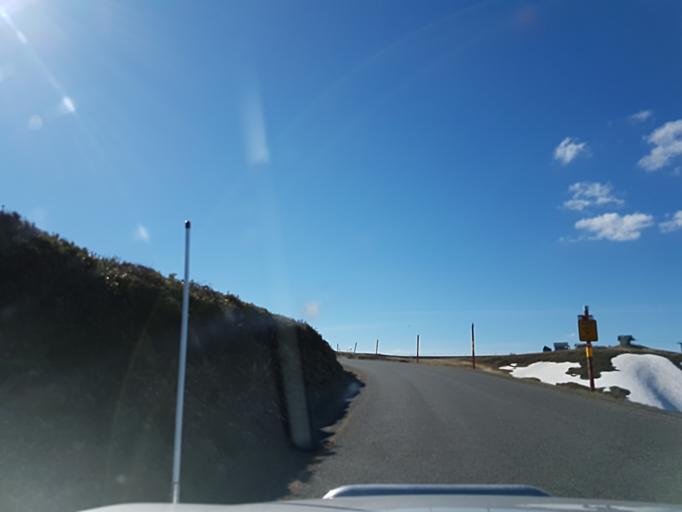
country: AU
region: Victoria
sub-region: Alpine
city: Mount Beauty
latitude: -36.9783
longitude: 147.1411
